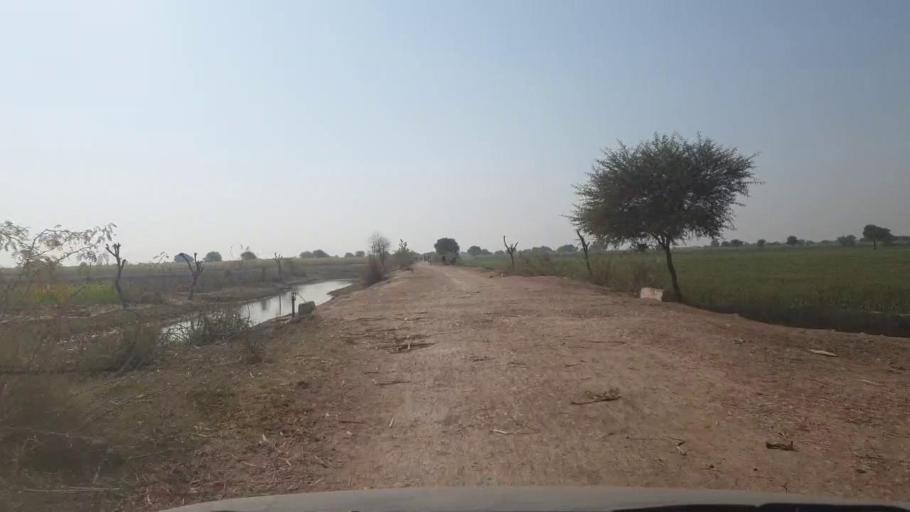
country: PK
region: Sindh
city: Chambar
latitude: 25.3641
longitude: 68.7651
